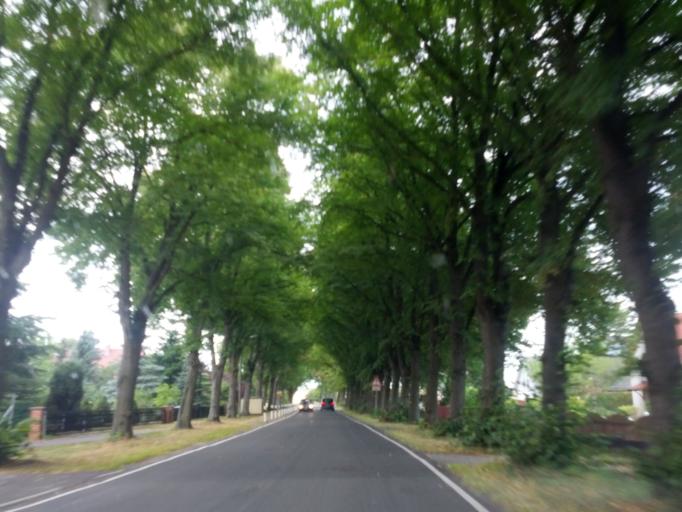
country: DE
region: Brandenburg
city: Kremmen
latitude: 52.7381
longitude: 12.9540
